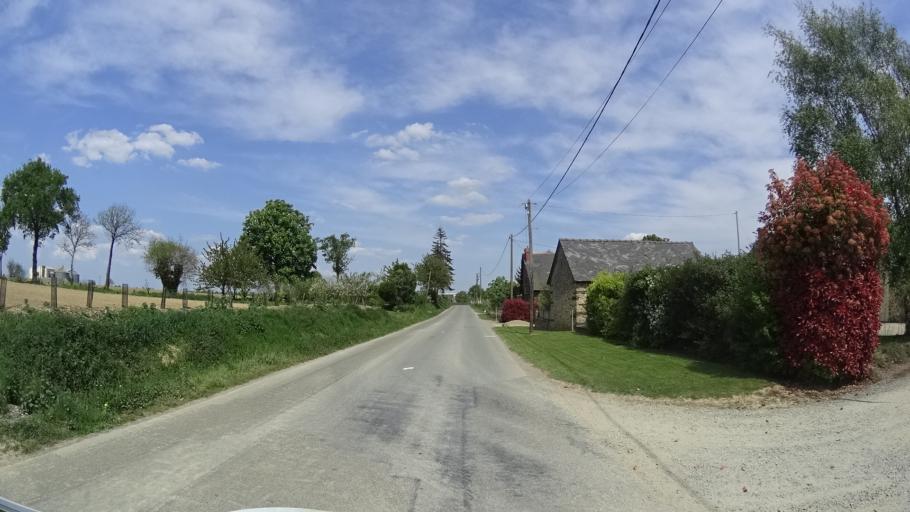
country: FR
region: Brittany
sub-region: Departement d'Ille-et-Vilaine
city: Torce
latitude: 48.0663
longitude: -1.2673
